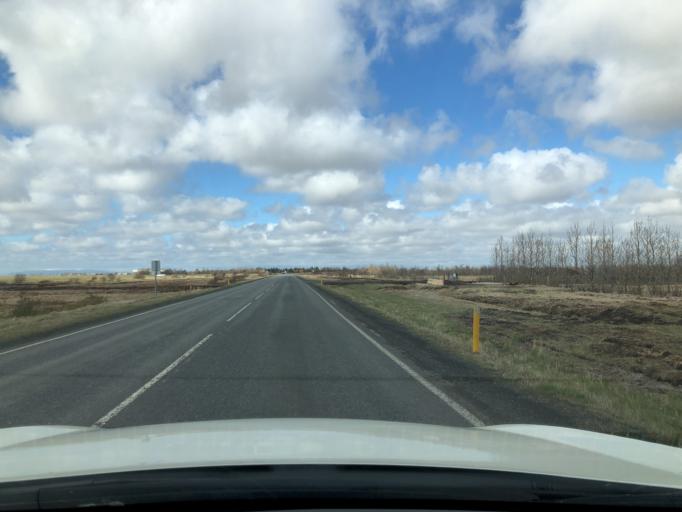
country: IS
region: South
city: Vestmannaeyjar
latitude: 63.7533
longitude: -20.2383
